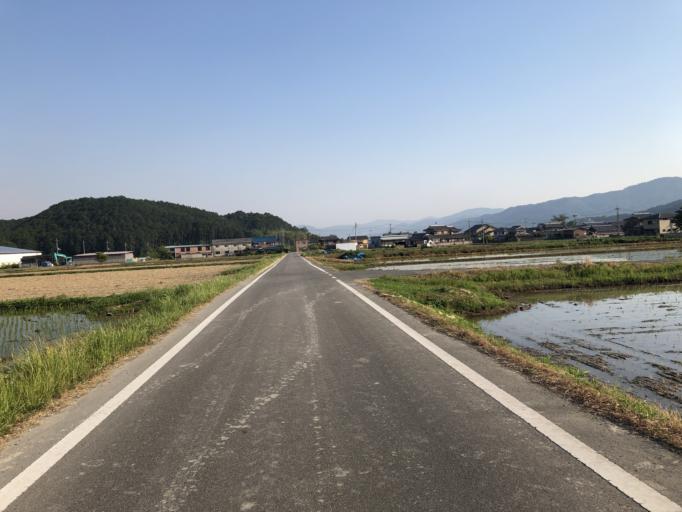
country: JP
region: Kyoto
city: Kameoka
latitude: 35.0744
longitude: 135.5568
